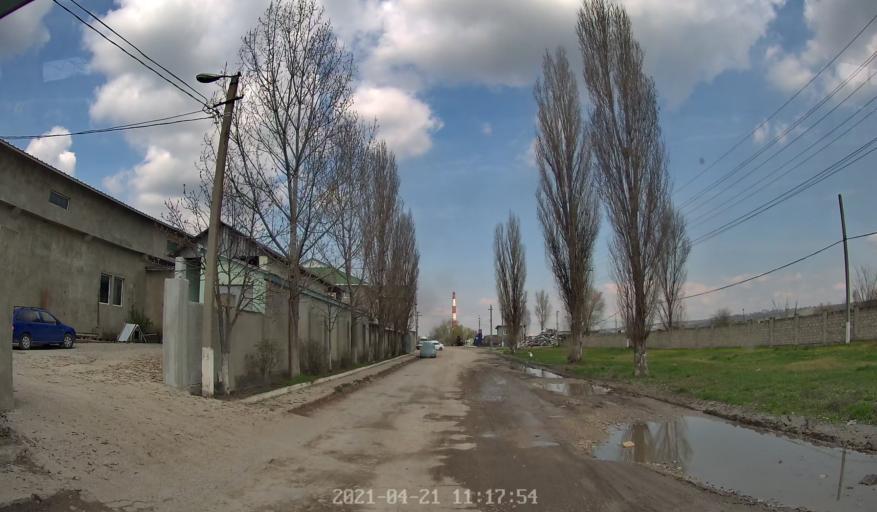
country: MD
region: Chisinau
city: Singera
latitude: 46.9576
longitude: 28.9266
